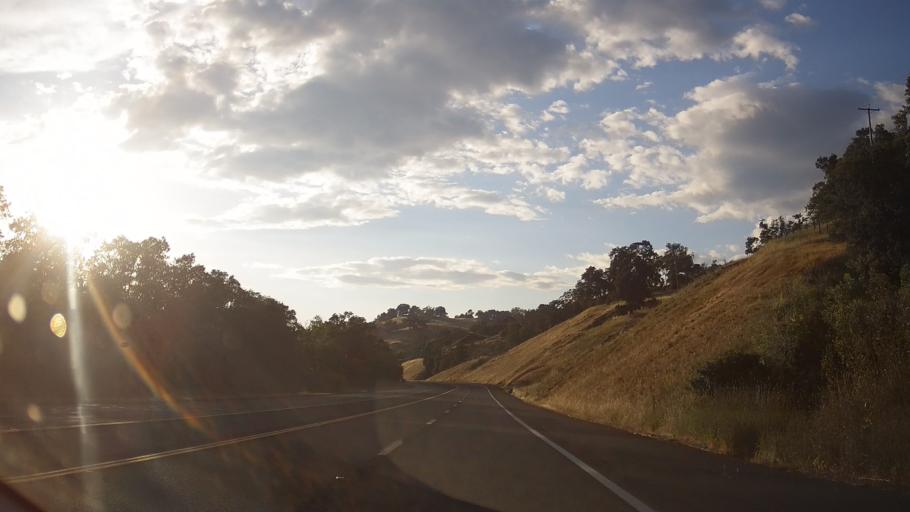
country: US
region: California
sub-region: Sonoma County
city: Cloverdale
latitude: 38.9357
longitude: -123.0640
